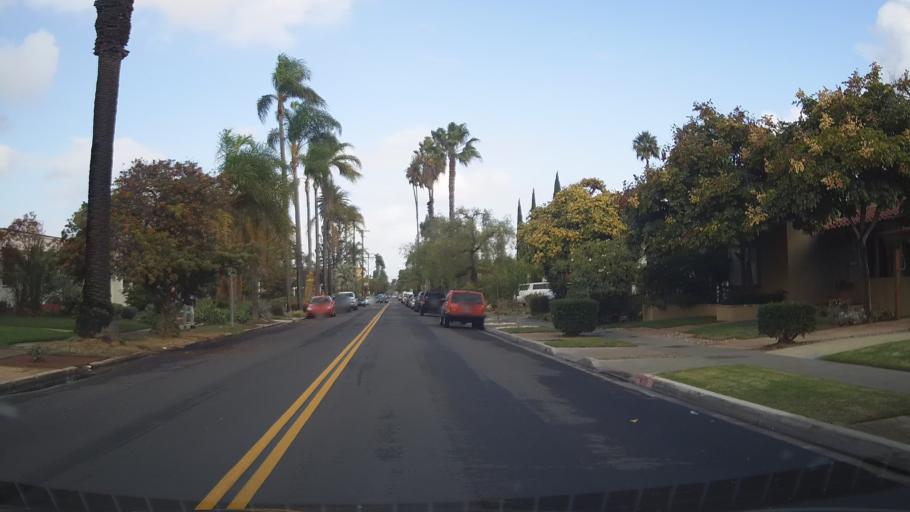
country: US
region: California
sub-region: San Diego County
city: San Diego
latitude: 32.7613
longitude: -117.1063
